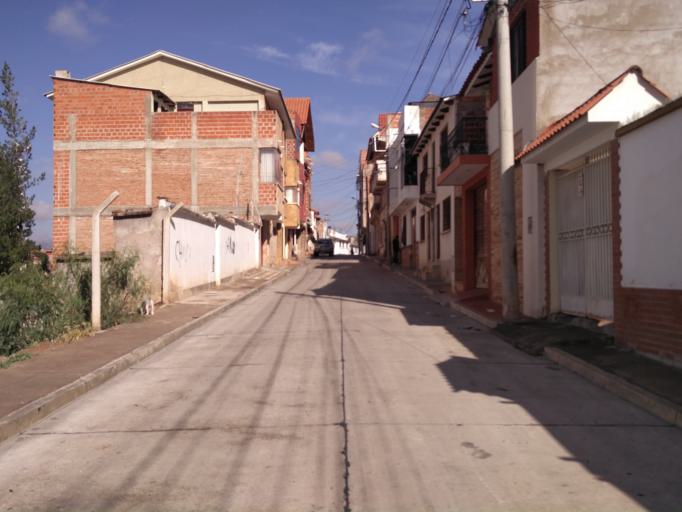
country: BO
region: Chuquisaca
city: Sucre
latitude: -19.0380
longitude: -65.2466
